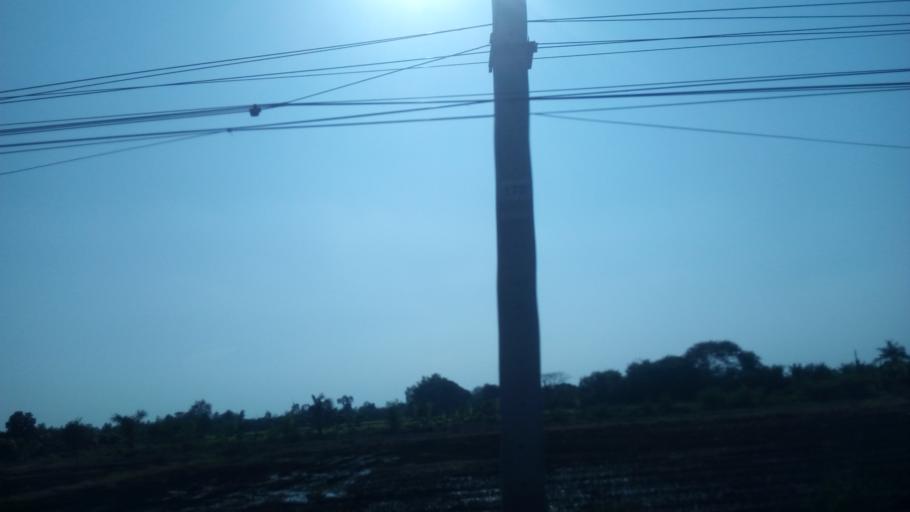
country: TH
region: Nonthaburi
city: Bang Yai
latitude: 13.8968
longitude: 100.3254
